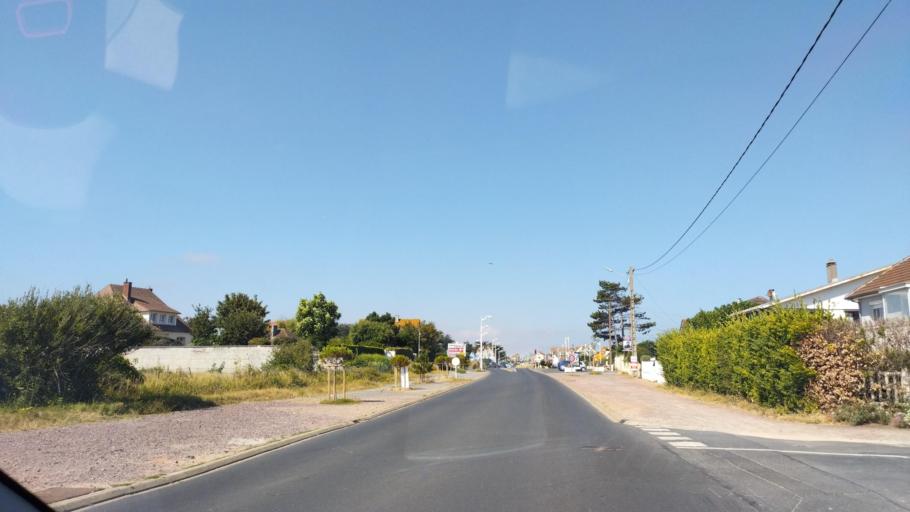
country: FR
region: Lower Normandy
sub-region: Departement du Calvados
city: Bernieres-sur-Mer
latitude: 49.3347
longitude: -0.4157
